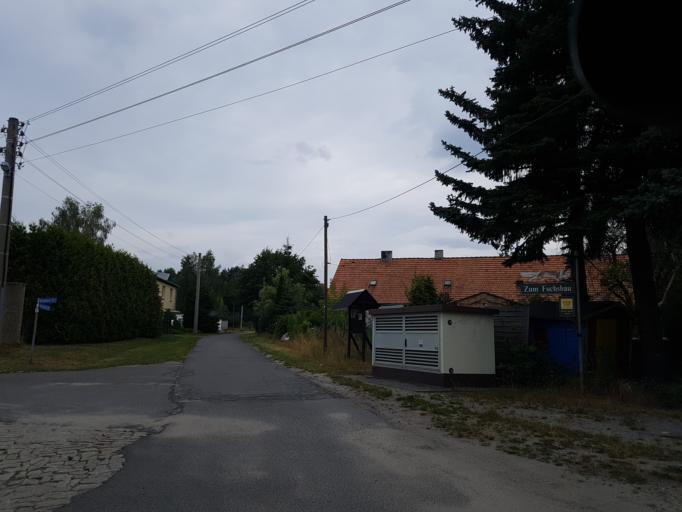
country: DE
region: Brandenburg
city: Sallgast
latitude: 51.5718
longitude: 13.8657
